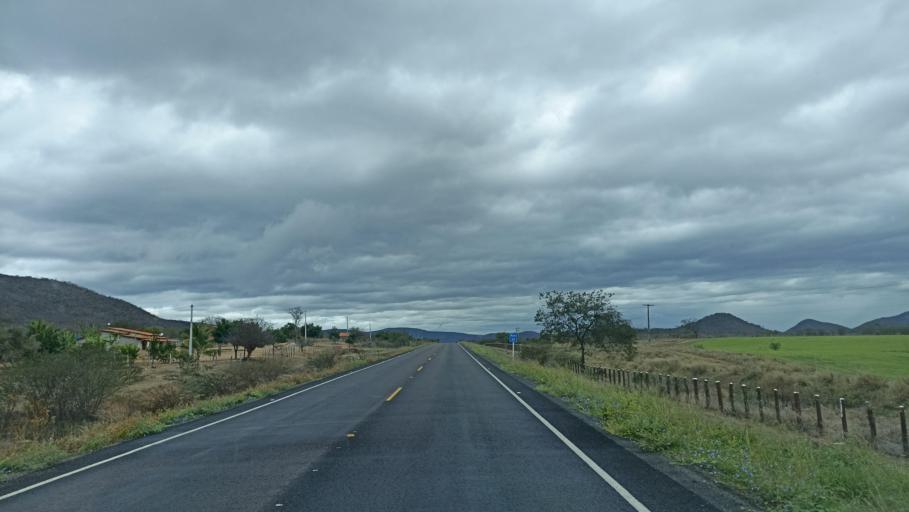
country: BR
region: Bahia
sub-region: Iacu
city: Iacu
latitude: -12.8948
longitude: -40.3988
